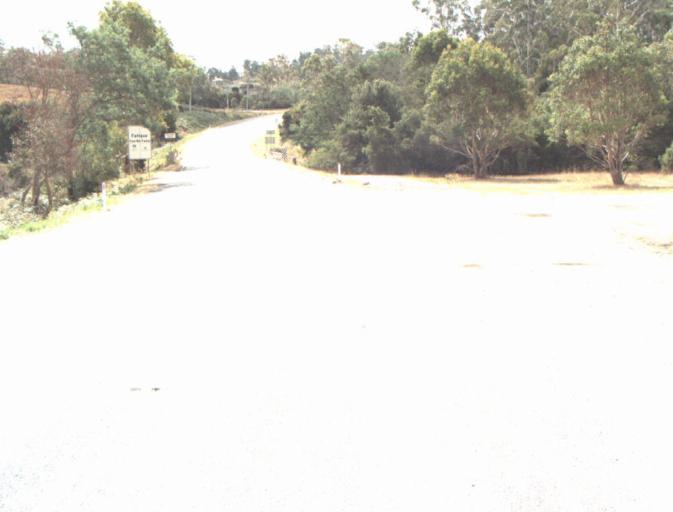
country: AU
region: Tasmania
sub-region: Launceston
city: Mayfield
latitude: -41.3085
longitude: 147.0504
